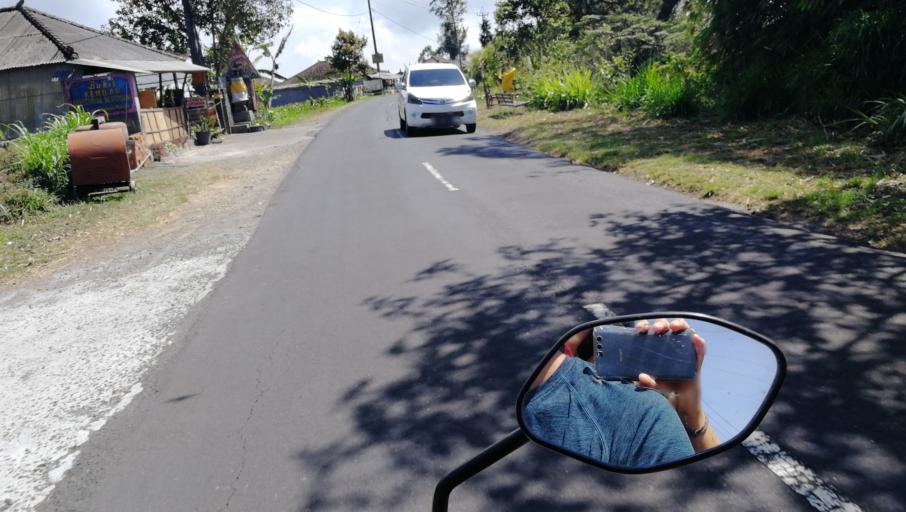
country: ID
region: Bali
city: Munduk
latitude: -8.2448
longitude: 115.1016
